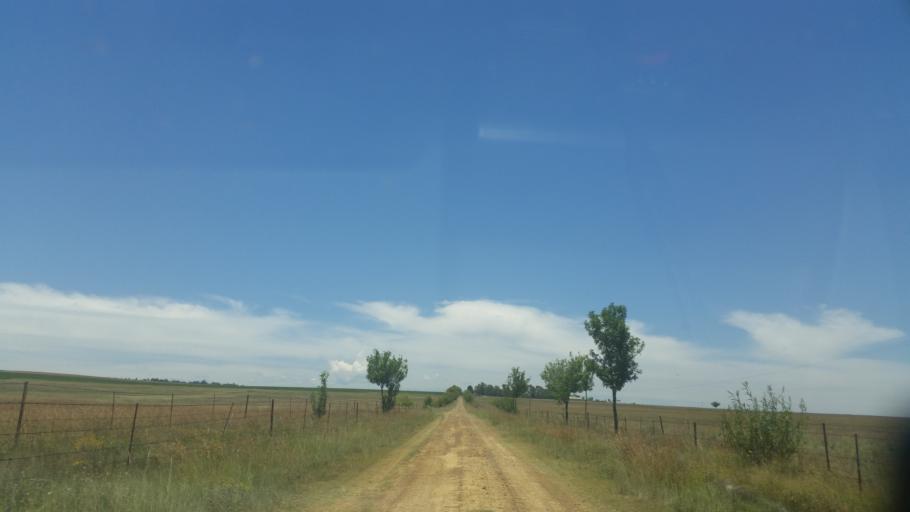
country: ZA
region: Orange Free State
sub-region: Thabo Mofutsanyana District Municipality
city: Harrismith
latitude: -28.1840
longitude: 29.0216
